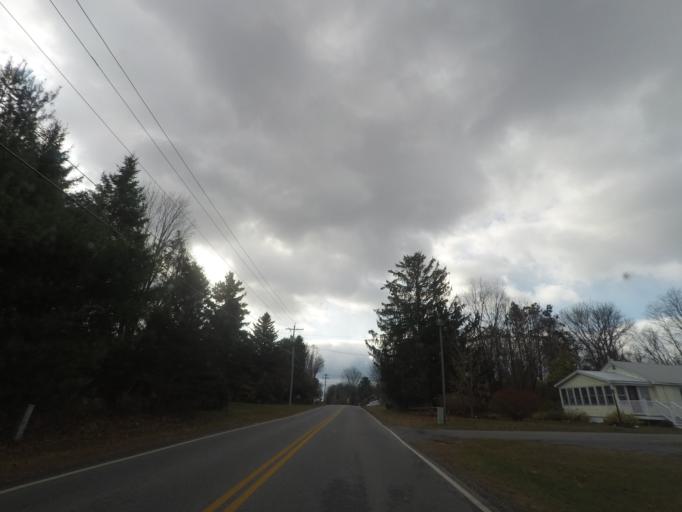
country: US
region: New York
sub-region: Saratoga County
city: Ballston Spa
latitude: 43.0005
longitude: -73.8108
